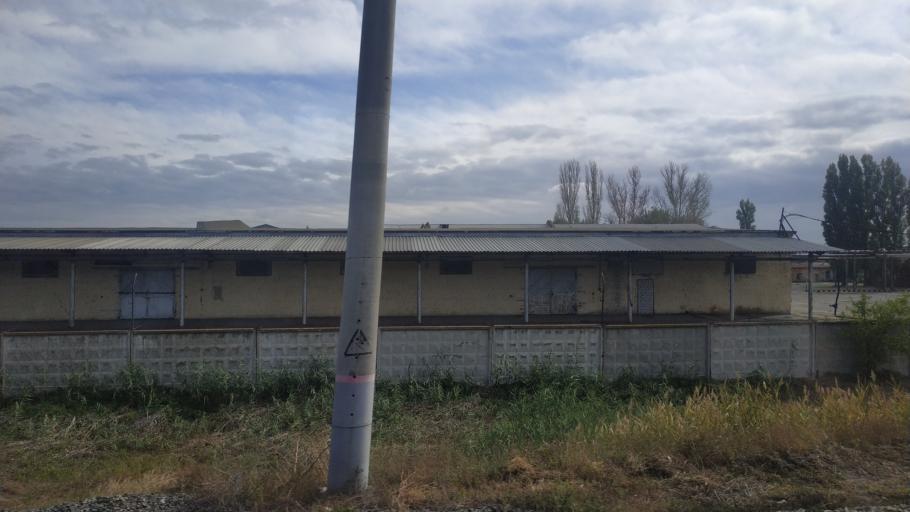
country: RU
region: Volgograd
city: Volgograd
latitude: 48.6041
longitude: 44.4347
